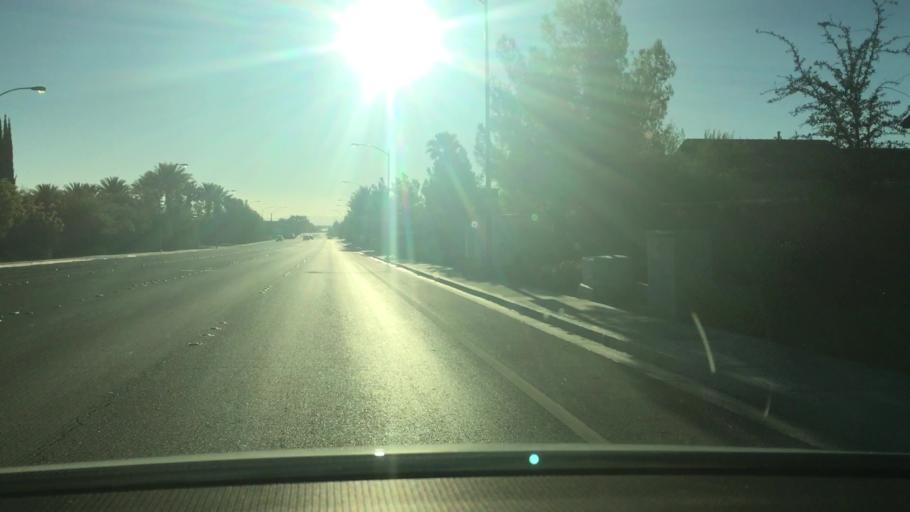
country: US
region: Nevada
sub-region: Clark County
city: Summerlin South
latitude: 36.0775
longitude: -115.3105
